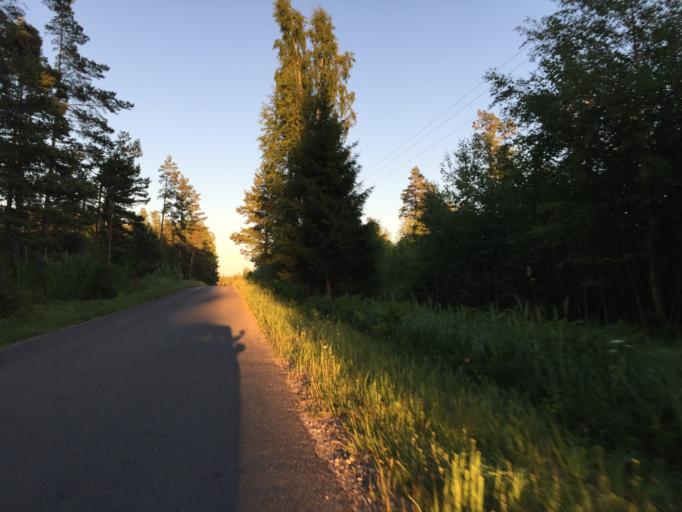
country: EE
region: Harju
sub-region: Kuusalu vald
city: Kuusalu
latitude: 59.5050
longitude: 25.2837
